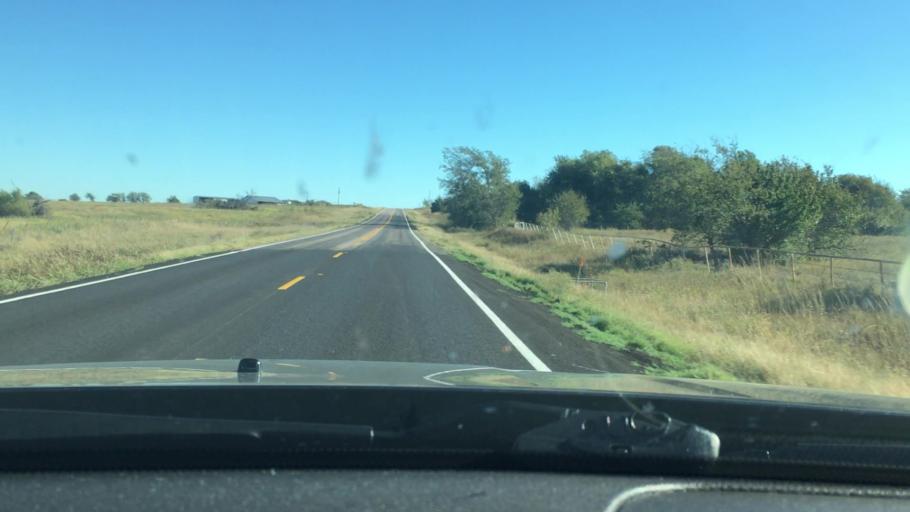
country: US
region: Oklahoma
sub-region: Marshall County
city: Madill
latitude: 34.1157
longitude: -96.7368
